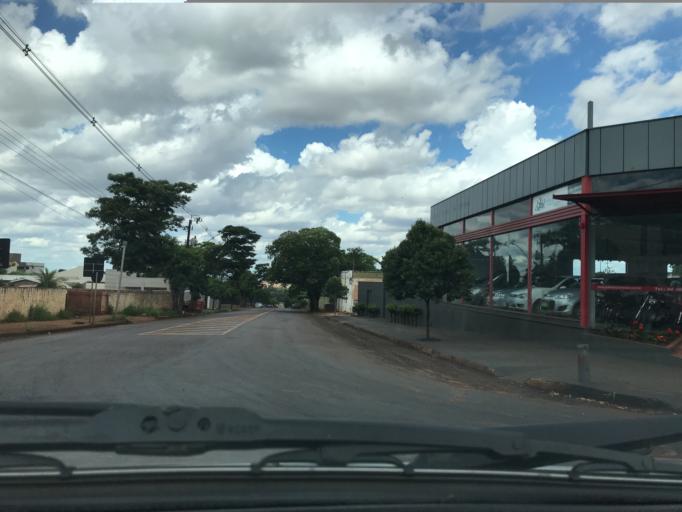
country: BR
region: Parana
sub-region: Palotina
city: Palotina
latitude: -24.2895
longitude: -53.8379
